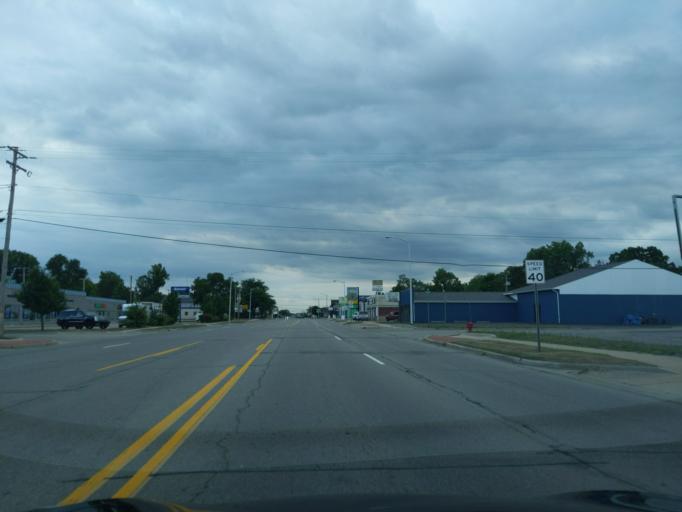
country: US
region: Michigan
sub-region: Isabella County
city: Mount Pleasant
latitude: 43.6113
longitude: -84.7678
